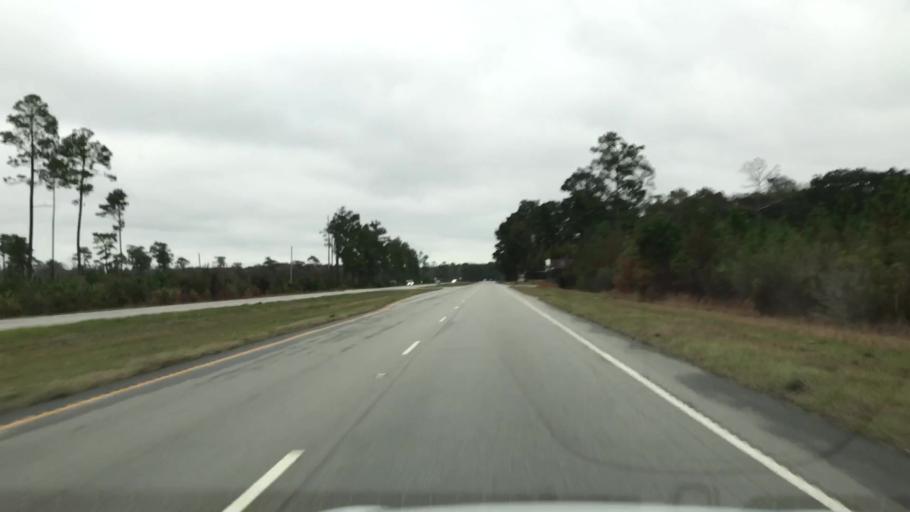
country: US
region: South Carolina
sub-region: Charleston County
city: Awendaw
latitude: 33.1723
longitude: -79.4182
